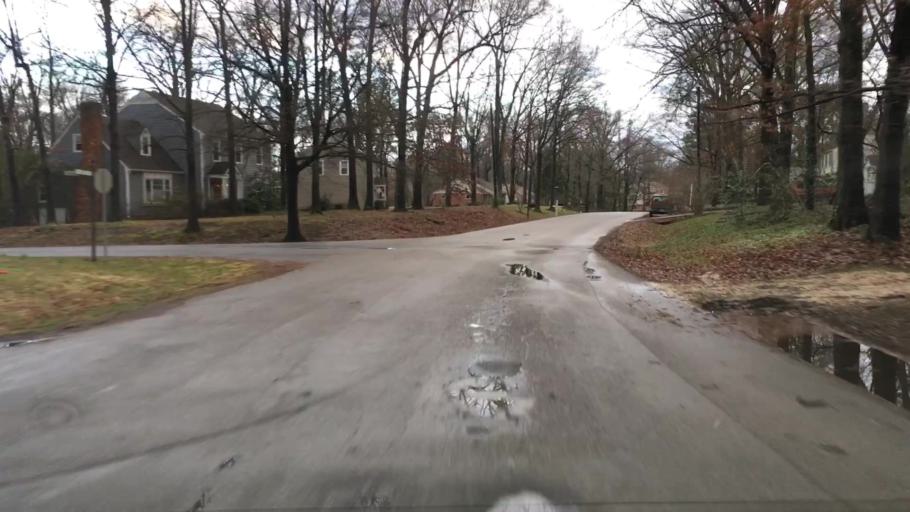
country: US
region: Virginia
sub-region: Chesterfield County
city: Bon Air
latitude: 37.5157
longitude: -77.6210
